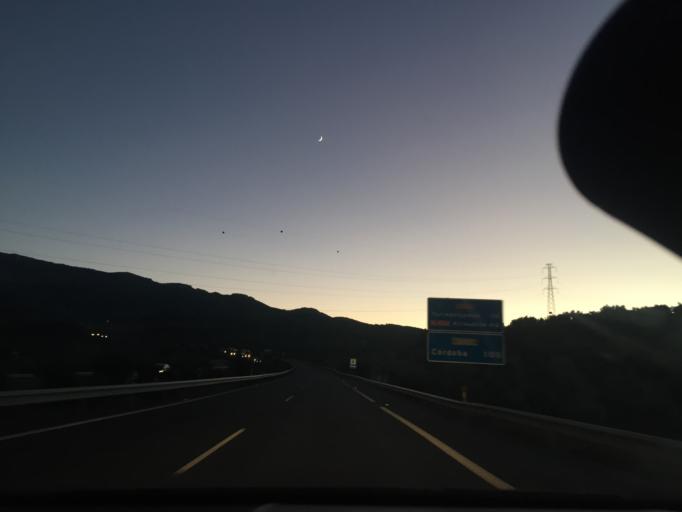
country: ES
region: Andalusia
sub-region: Provincia de Jaen
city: Jaen
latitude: 37.7989
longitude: -3.8230
